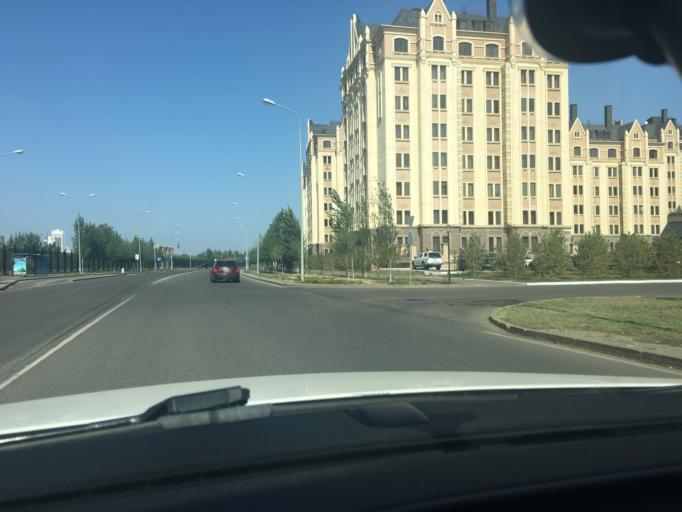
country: KZ
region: Astana Qalasy
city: Astana
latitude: 51.1147
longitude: 71.4548
